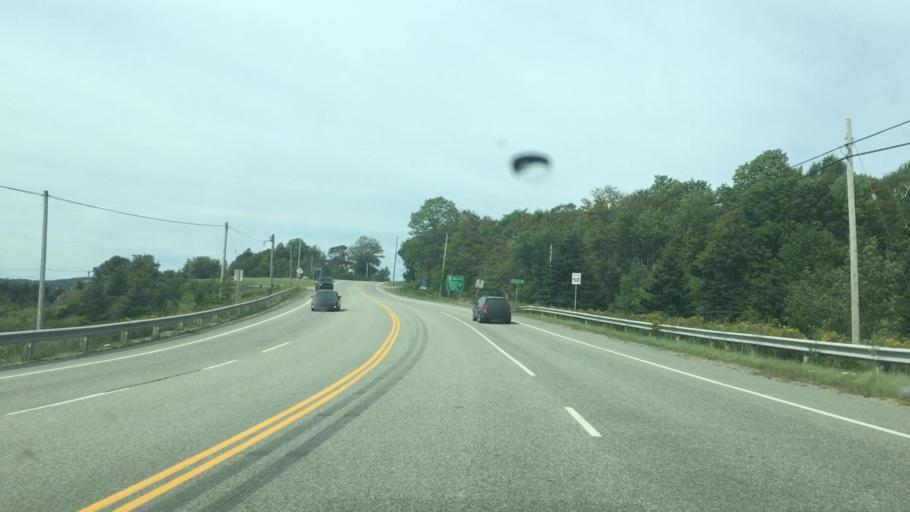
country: CA
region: Nova Scotia
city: Port Hawkesbury
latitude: 45.6444
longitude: -61.3970
